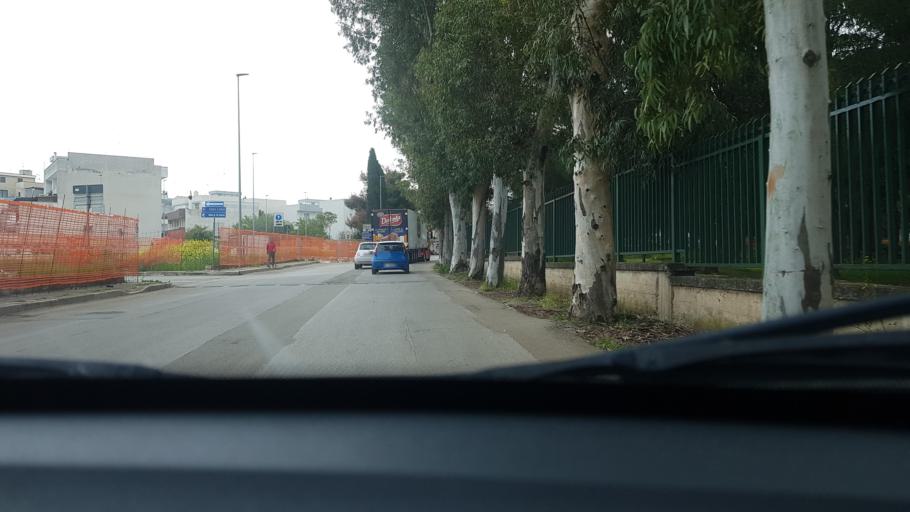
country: IT
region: Apulia
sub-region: Provincia di Bari
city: Noicattaro
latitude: 41.0367
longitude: 16.9824
